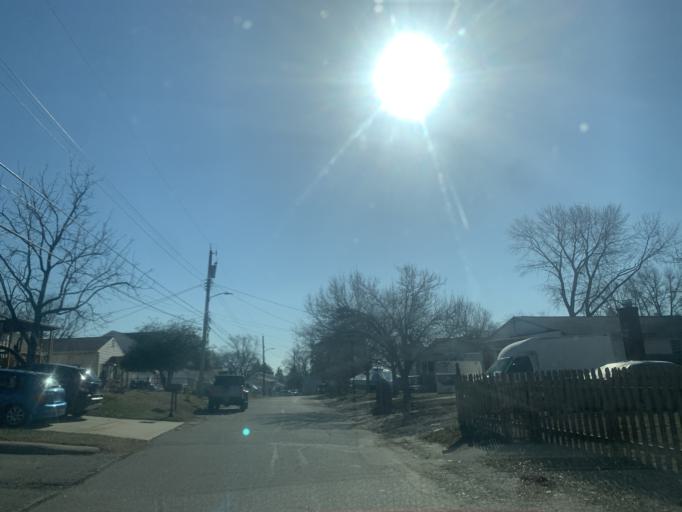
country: US
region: Maryland
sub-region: Anne Arundel County
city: Riviera Beach
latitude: 39.1685
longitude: -76.5265
